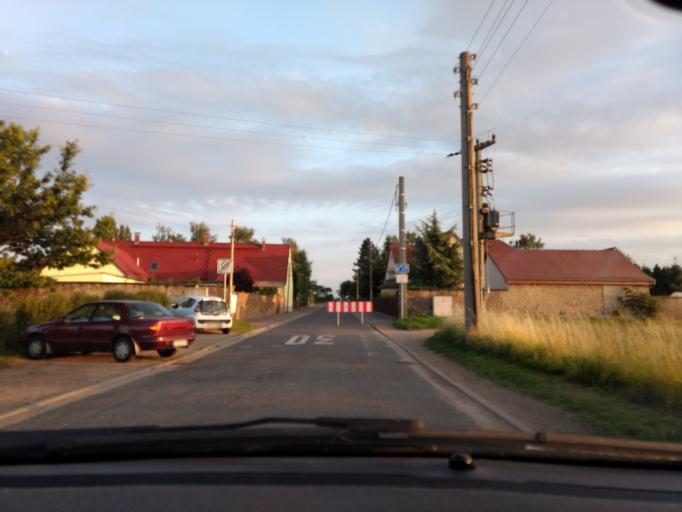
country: DE
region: Saxony
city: Radebeul
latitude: 51.1154
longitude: 13.6683
